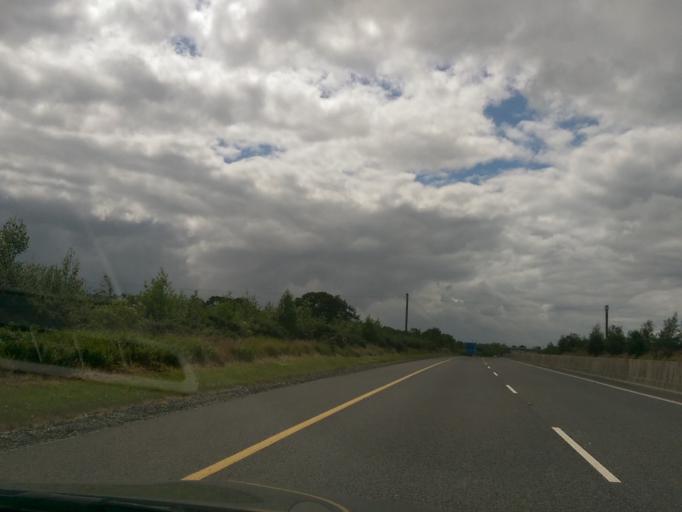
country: IE
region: Munster
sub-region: County Cork
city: Mitchelstown
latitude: 52.2515
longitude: -8.2594
